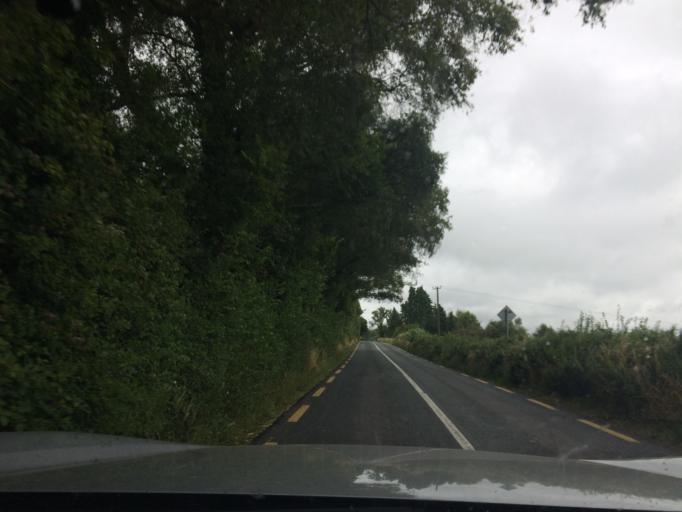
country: IE
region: Munster
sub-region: South Tipperary
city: Cluain Meala
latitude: 52.2923
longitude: -7.7730
